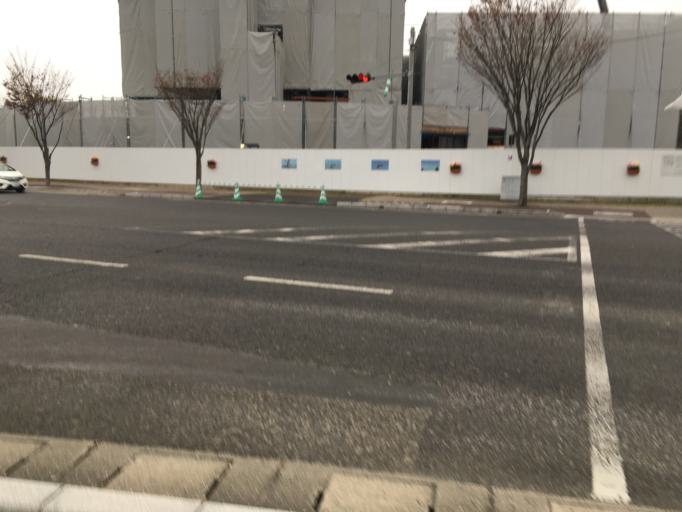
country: JP
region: Saga Prefecture
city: Saga-shi
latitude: 33.2552
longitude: 130.2930
